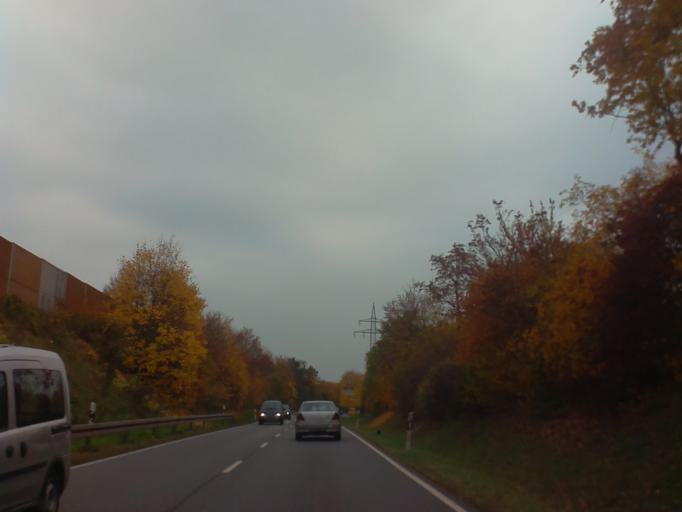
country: DE
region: Baden-Wuerttemberg
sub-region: Karlsruhe Region
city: Ilvesheim
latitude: 49.4856
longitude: 8.5476
